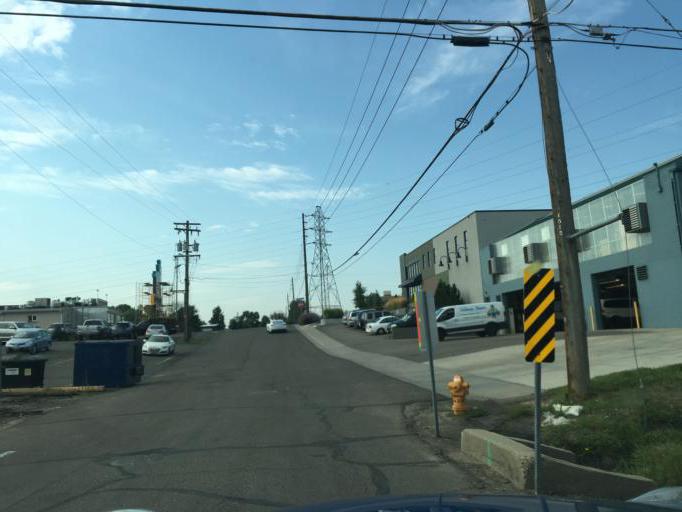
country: US
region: Colorado
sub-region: Jefferson County
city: Wheat Ridge
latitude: 39.7412
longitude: -105.1037
